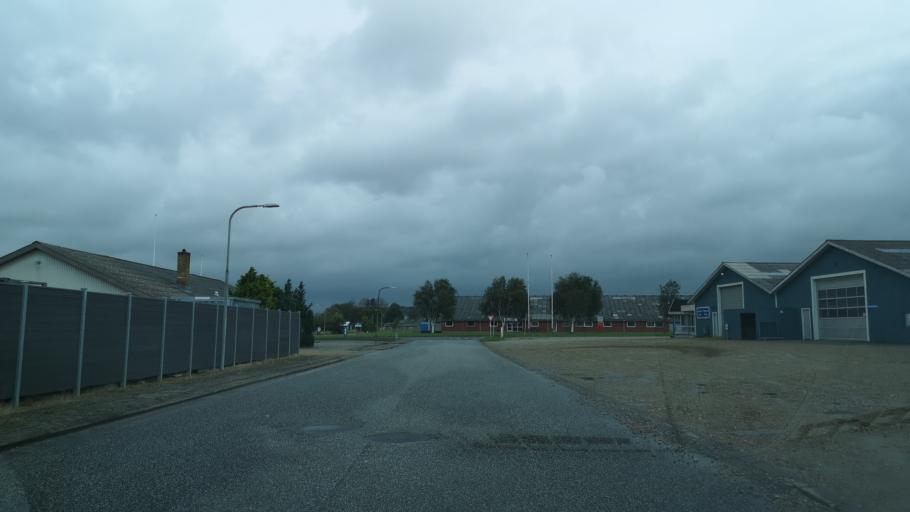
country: DK
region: Central Jutland
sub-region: Ringkobing-Skjern Kommune
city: Videbaek
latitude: 56.0886
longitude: 8.6459
